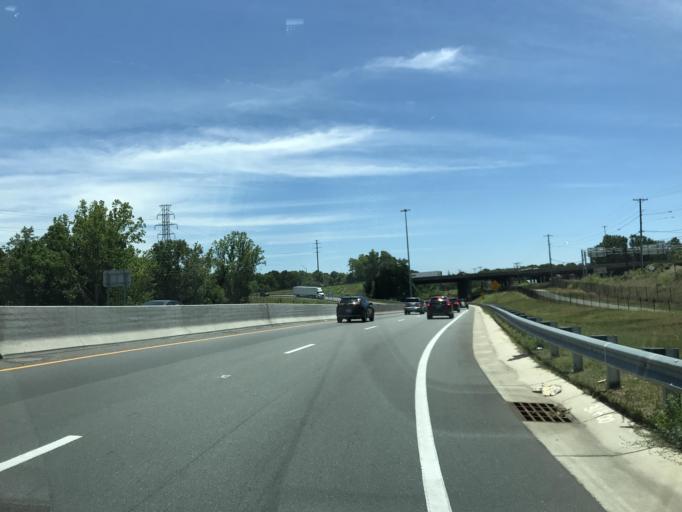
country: US
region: North Carolina
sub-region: Gaston County
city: Gastonia
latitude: 35.2859
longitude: -81.1872
